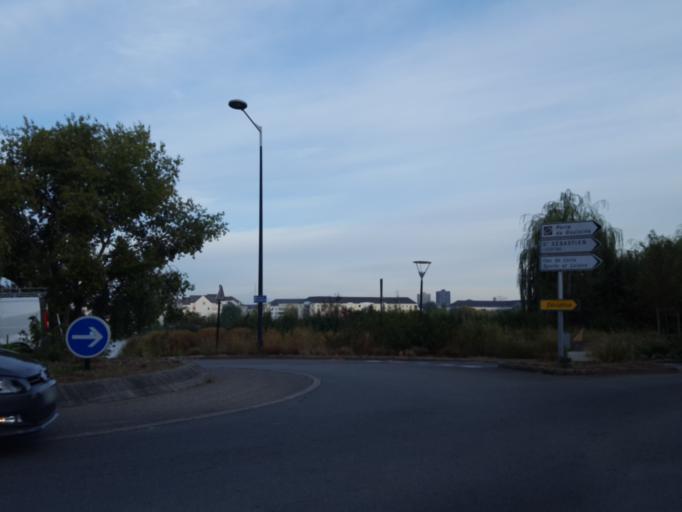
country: FR
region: Pays de la Loire
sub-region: Departement de la Loire-Atlantique
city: Saint-Sebastien-sur-Loire
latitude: 47.2050
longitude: -1.5226
